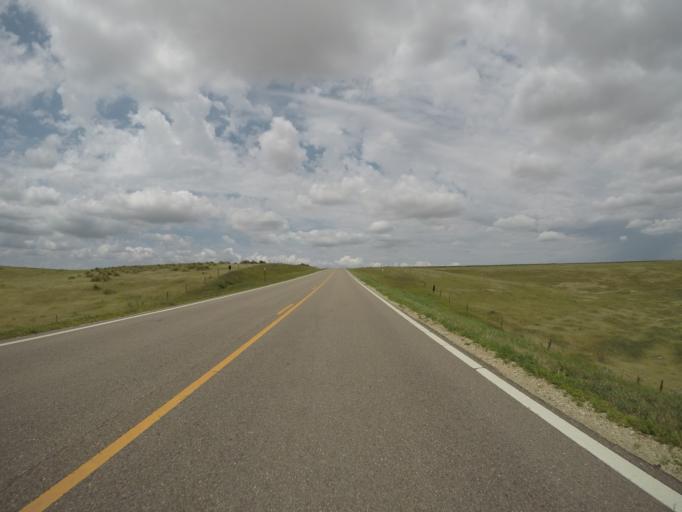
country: US
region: Kansas
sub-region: Rawlins County
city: Atwood
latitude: 39.6983
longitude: -101.0564
